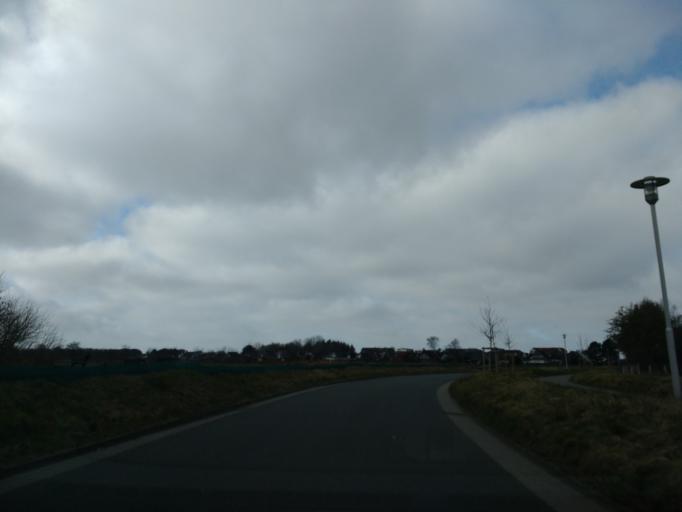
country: DE
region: Lower Saxony
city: Cuxhaven
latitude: 53.8772
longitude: 8.6299
